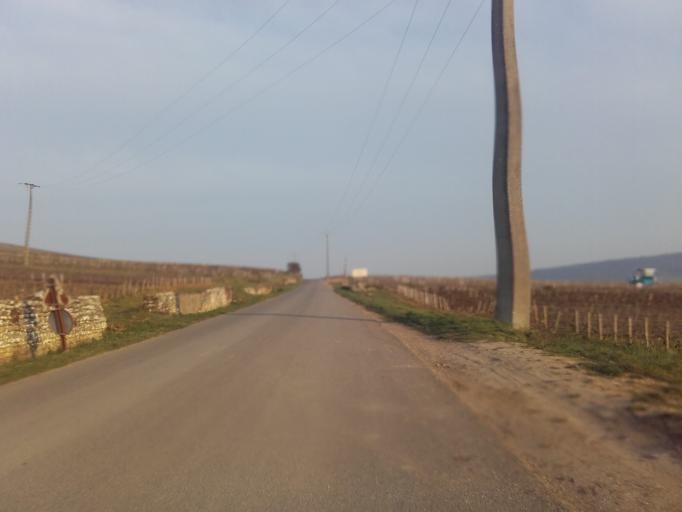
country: FR
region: Bourgogne
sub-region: Departement de la Cote-d'Or
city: Nolay
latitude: 46.9102
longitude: 4.6578
